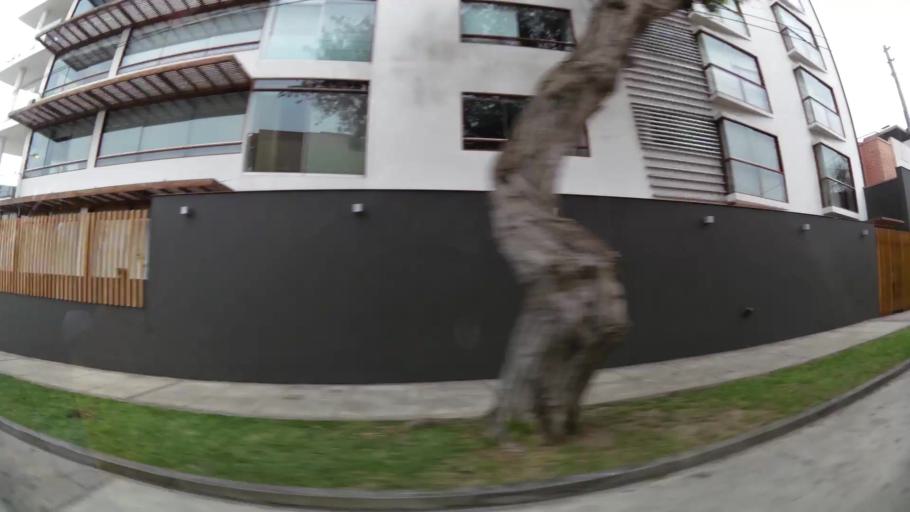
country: PE
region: Lima
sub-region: Lima
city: Surco
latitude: -12.1425
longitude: -77.0249
